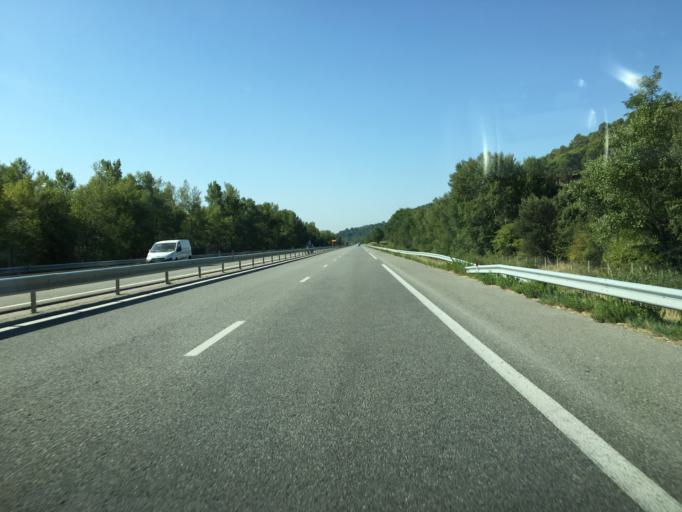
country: FR
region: Provence-Alpes-Cote d'Azur
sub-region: Departement des Alpes-de-Haute-Provence
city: Peyruis
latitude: 43.9964
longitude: 5.9190
